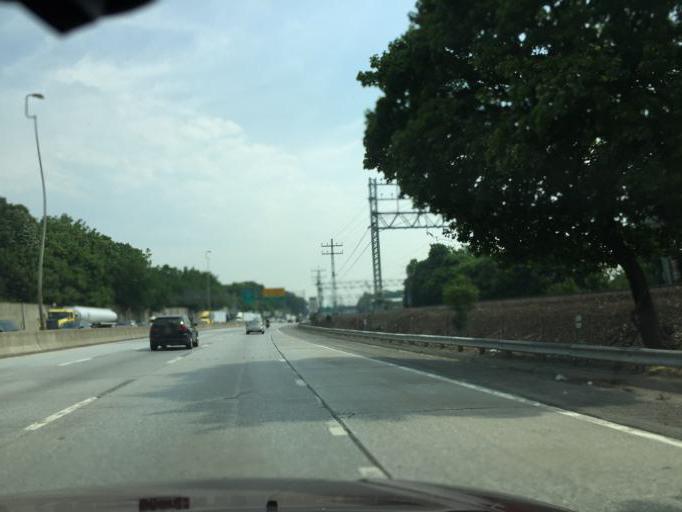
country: US
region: New York
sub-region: Westchester County
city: New Rochelle
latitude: 40.9205
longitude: -73.7771
